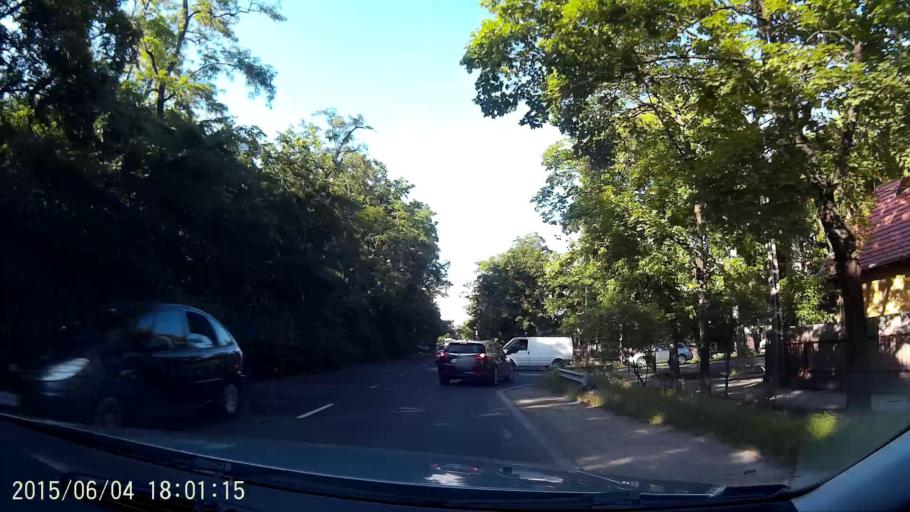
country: HU
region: Budapest
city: Budapest XX. keruelet
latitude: 47.4566
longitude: 19.1166
